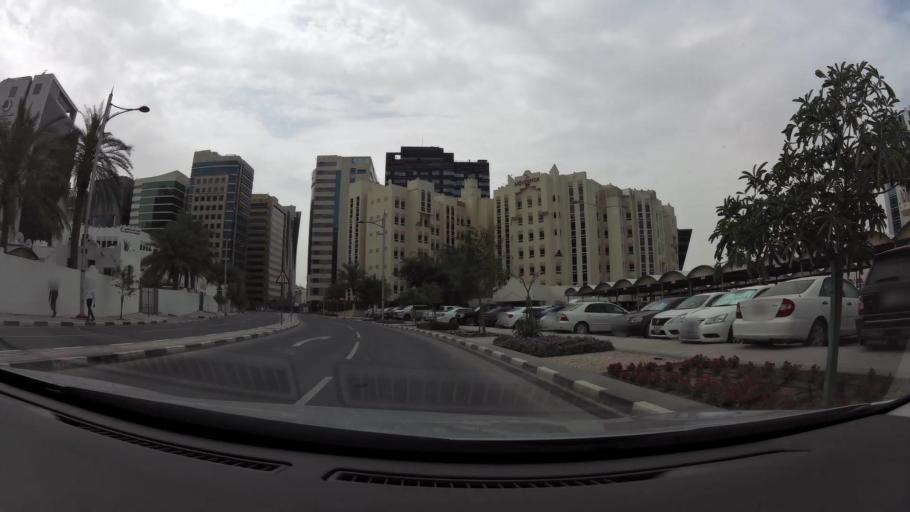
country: QA
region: Baladiyat ad Dawhah
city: Doha
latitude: 25.2899
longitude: 51.5456
